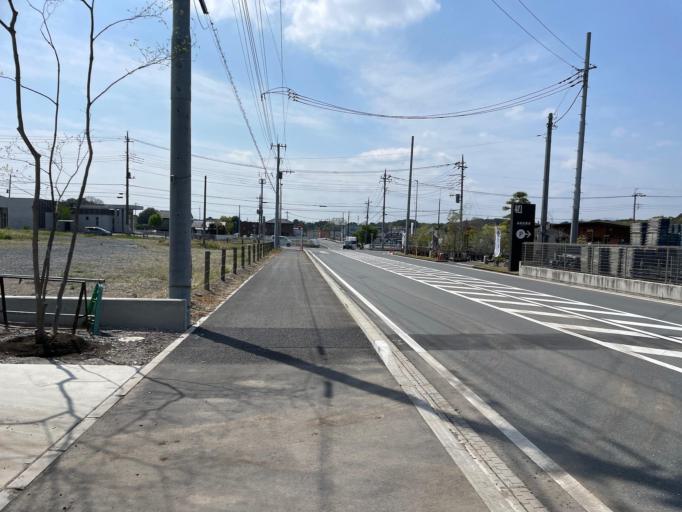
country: JP
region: Gunma
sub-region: Sawa-gun
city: Tamamura
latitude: 36.3044
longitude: 139.0858
